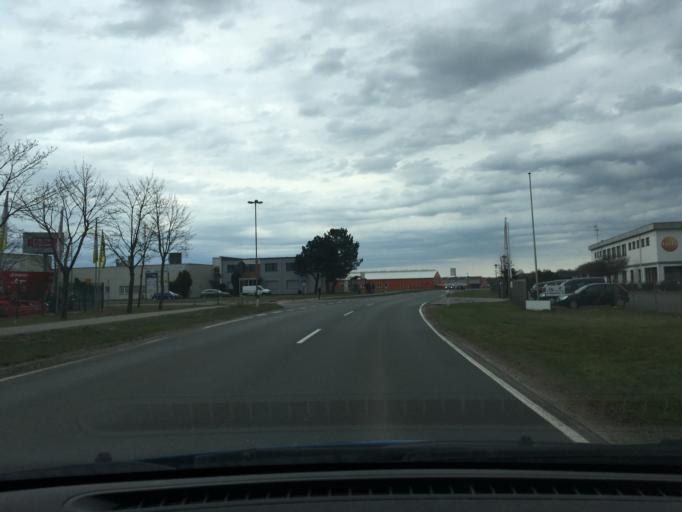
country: DE
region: Lower Saxony
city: Winsen
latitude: 53.3726
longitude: 10.2291
